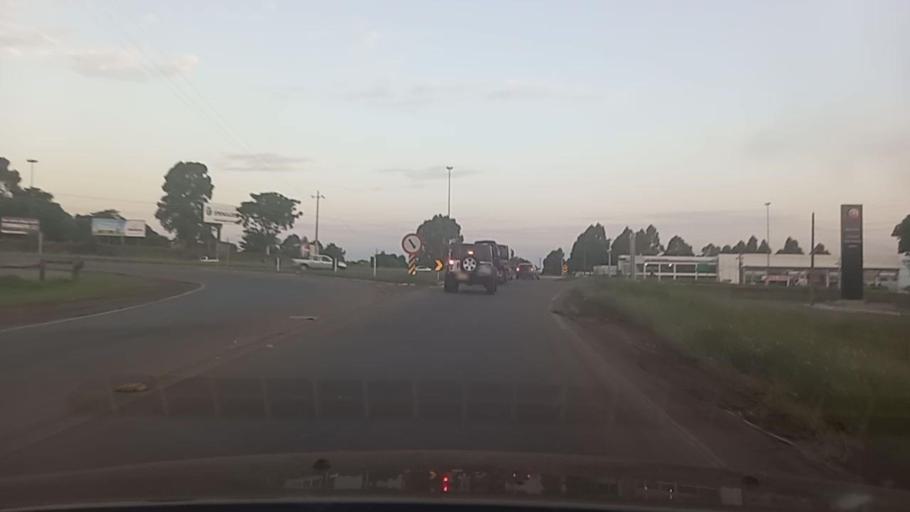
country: BR
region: Rio Grande do Sul
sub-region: Passo Fundo
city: Passo Fundo
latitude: -28.2698
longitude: -52.4414
